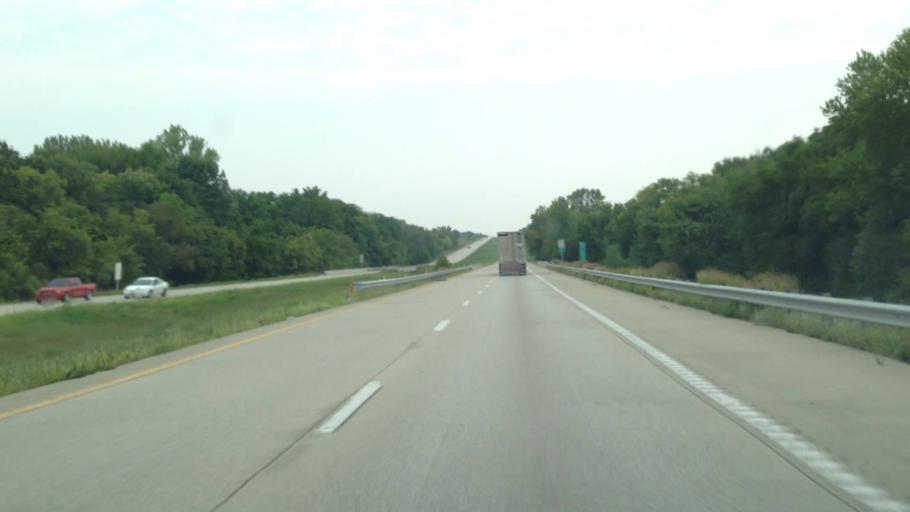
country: US
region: Missouri
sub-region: Clay County
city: Kearney
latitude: 39.4108
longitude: -94.3490
